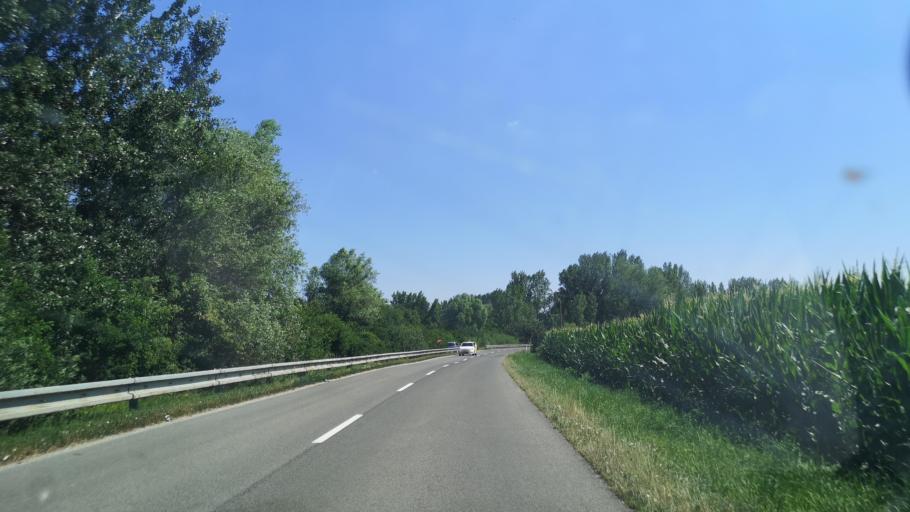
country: SK
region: Trnavsky
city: Dunajska Streda
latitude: 48.0436
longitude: 17.5606
